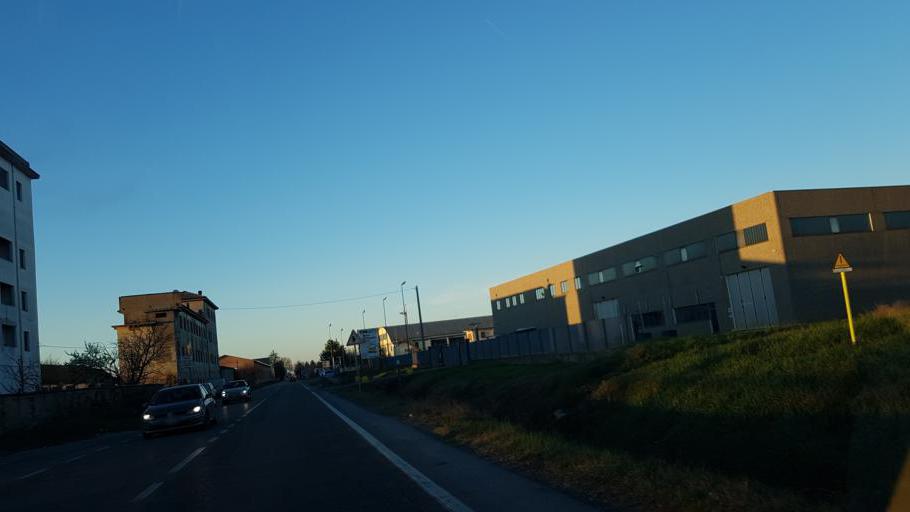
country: IT
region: Piedmont
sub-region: Provincia di Alessandria
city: Carbonara Scrivia
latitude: 44.8555
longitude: 8.8545
